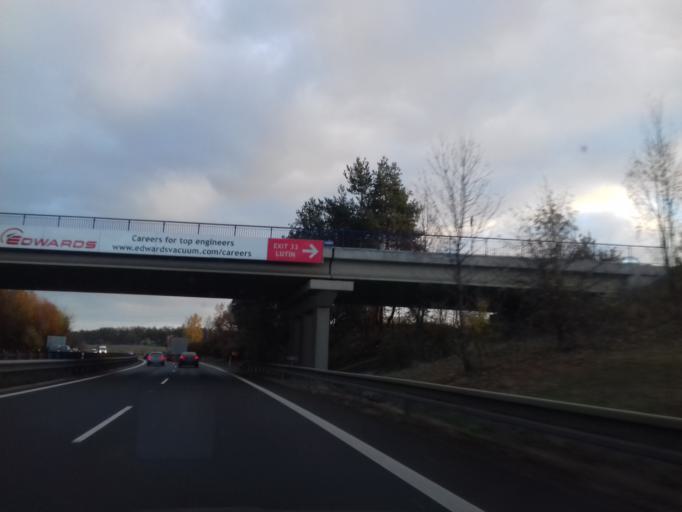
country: CZ
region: Olomoucky
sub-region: Okres Prostejov
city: Prostejov
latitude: 49.4901
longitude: 17.1411
